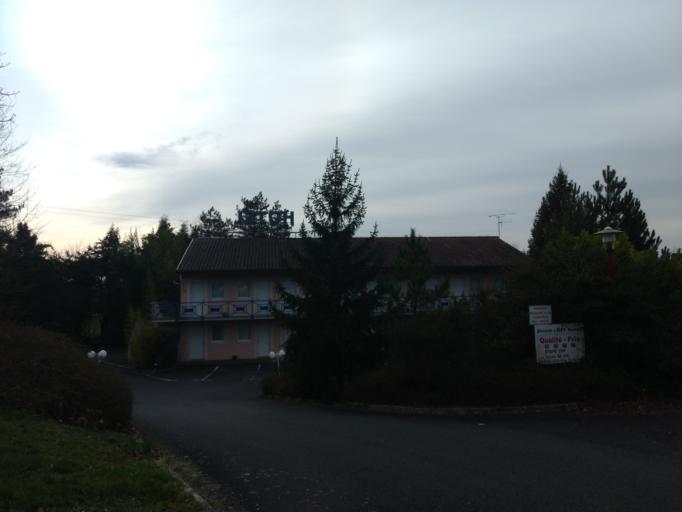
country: FR
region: Midi-Pyrenees
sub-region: Departement de l'Aveyron
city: Villeneuve
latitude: 44.3974
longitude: 2.0769
